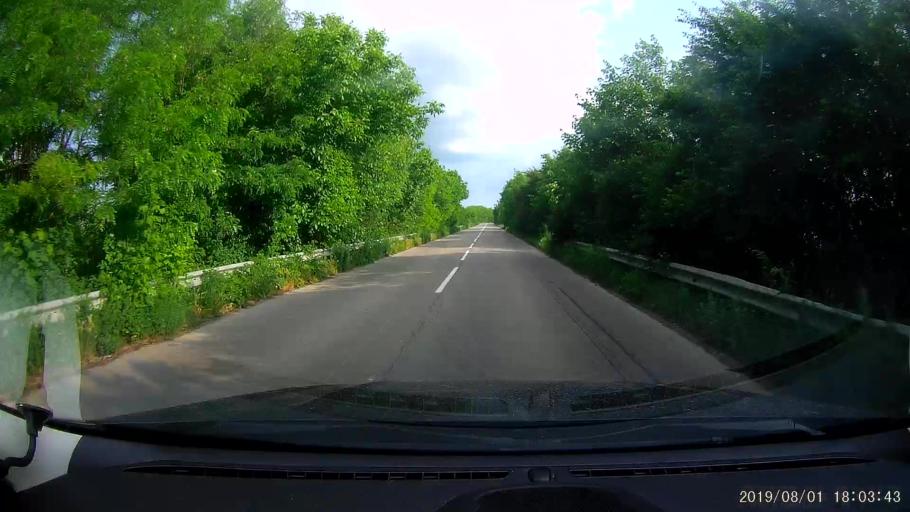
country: BG
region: Silistra
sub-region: Obshtina Alfatar
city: Alfatar
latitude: 43.9210
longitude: 27.2895
